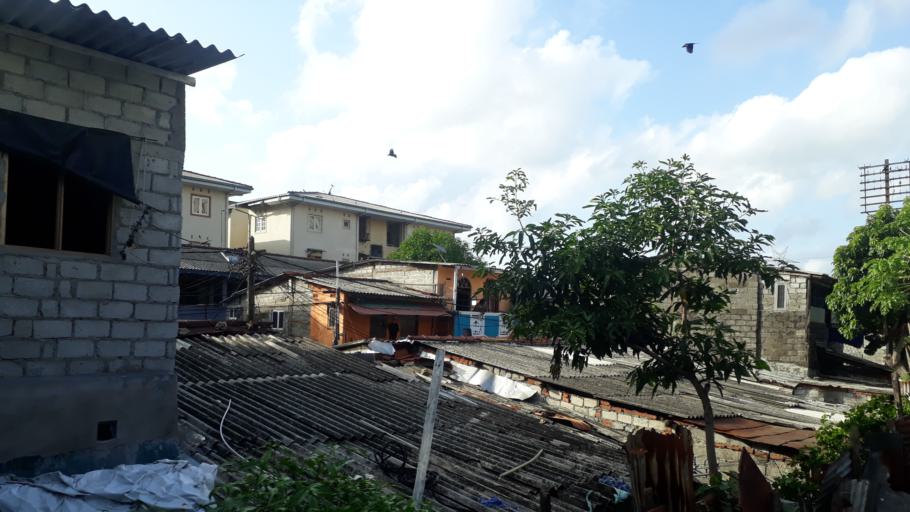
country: LK
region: Western
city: Kolonnawa
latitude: 6.9386
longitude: 79.8801
